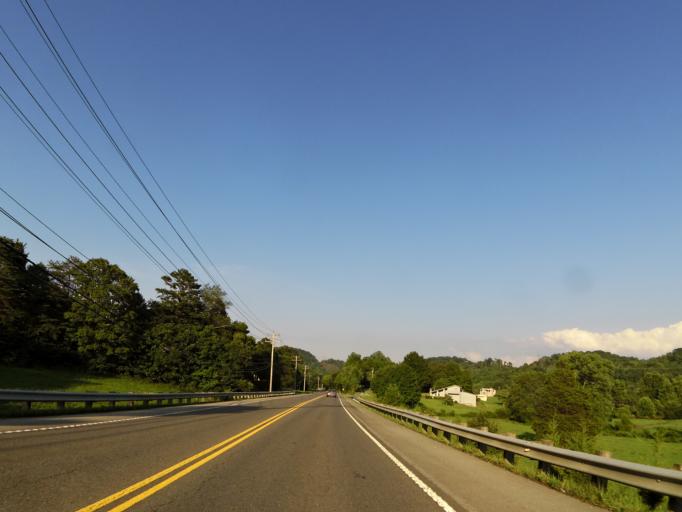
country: US
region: Tennessee
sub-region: Anderson County
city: Clinton
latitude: 36.0373
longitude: -84.1236
